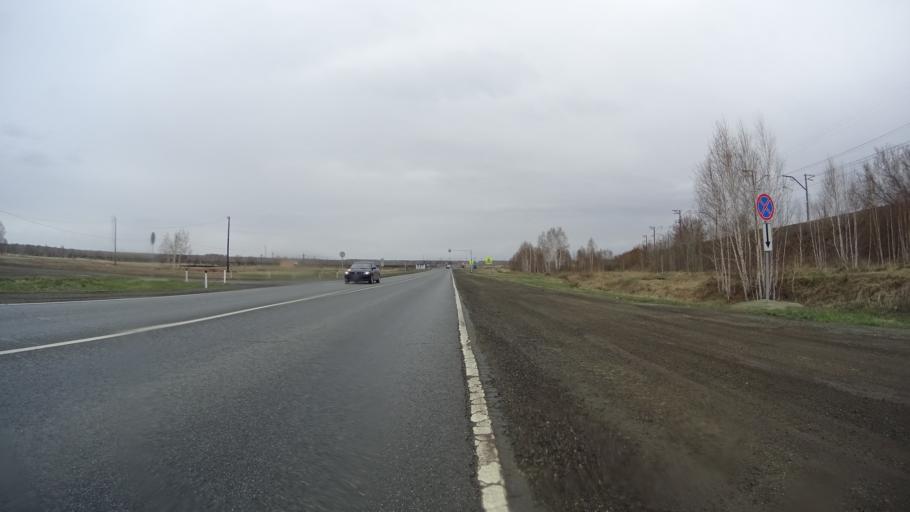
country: RU
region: Chelyabinsk
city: Krasnogorskiy
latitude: 54.6241
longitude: 61.2793
